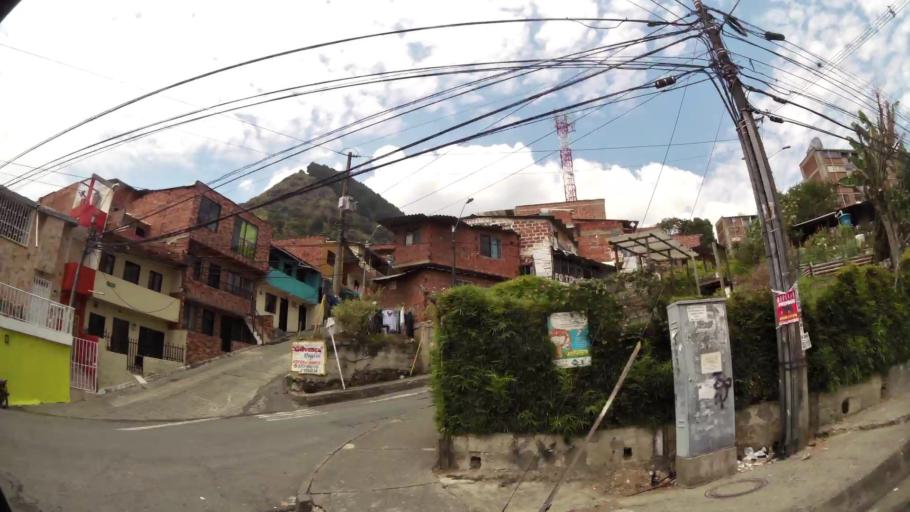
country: CO
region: Antioquia
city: Bello
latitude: 6.3045
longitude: -75.5819
